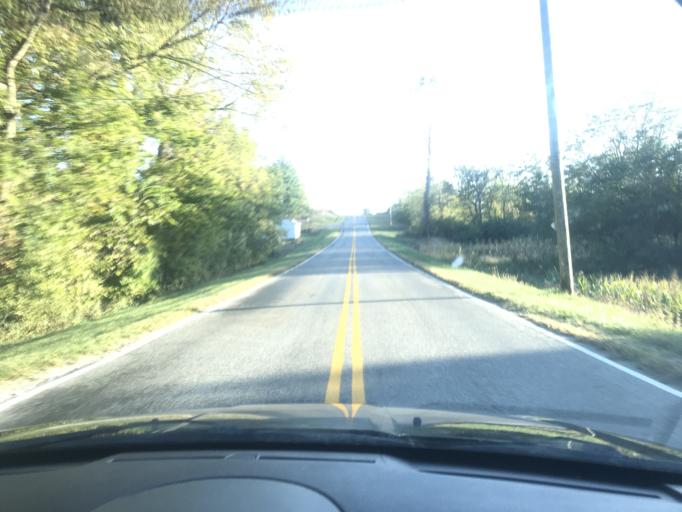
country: US
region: Ohio
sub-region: Logan County
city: De Graff
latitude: 40.2364
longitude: -83.8630
